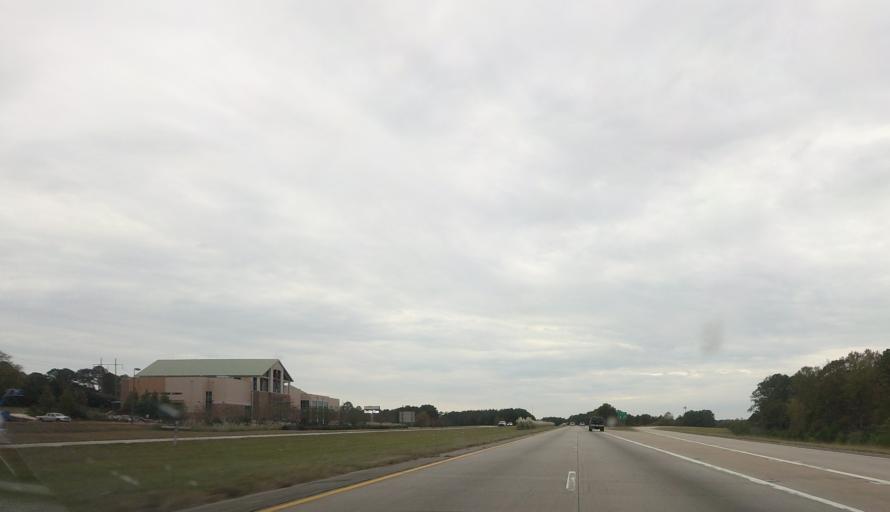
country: US
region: Alabama
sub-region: Russell County
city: Phenix City
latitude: 32.5241
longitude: -84.9827
